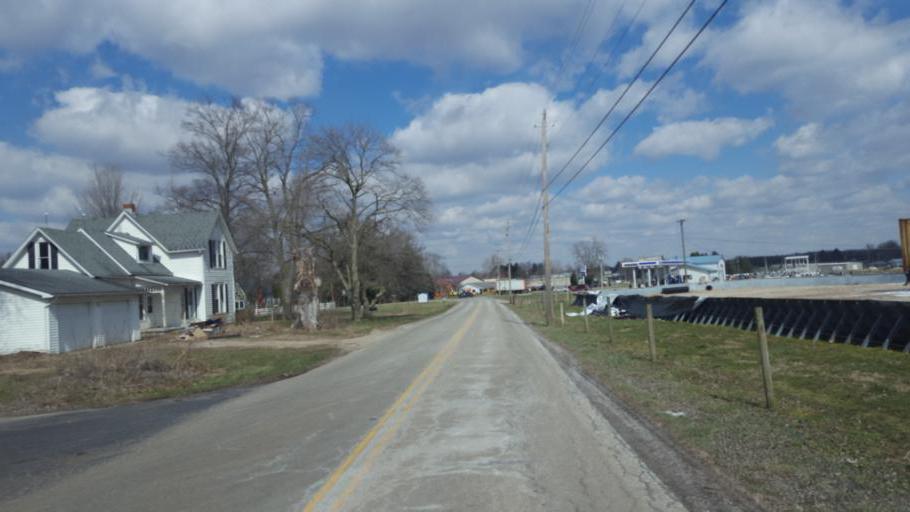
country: US
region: Ohio
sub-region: Knox County
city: Mount Vernon
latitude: 40.3698
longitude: -82.5105
